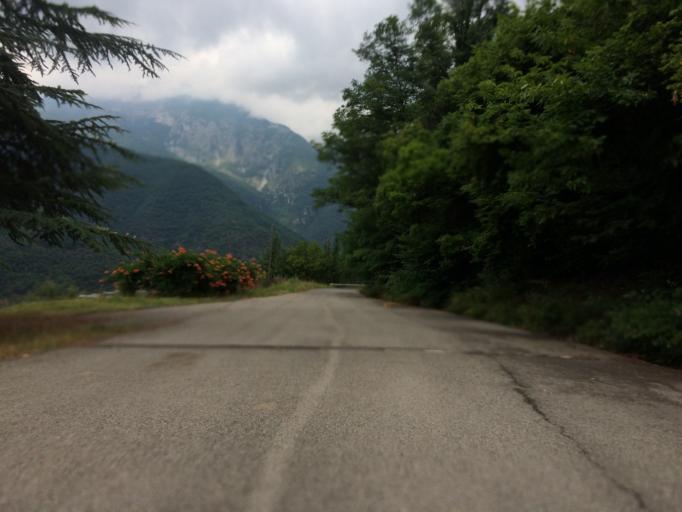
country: IT
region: Liguria
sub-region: Provincia di Imperia
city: Castel Vittorio
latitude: 43.9424
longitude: 7.6906
